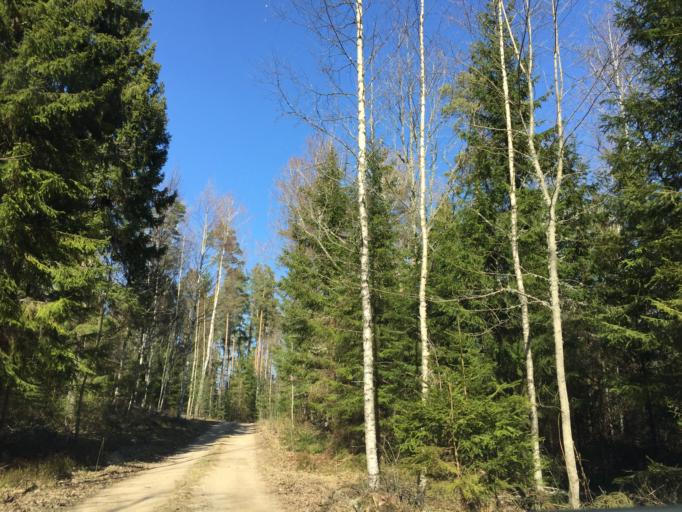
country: EE
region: Viljandimaa
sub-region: Viljandi linn
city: Viljandi
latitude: 58.2702
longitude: 25.6025
